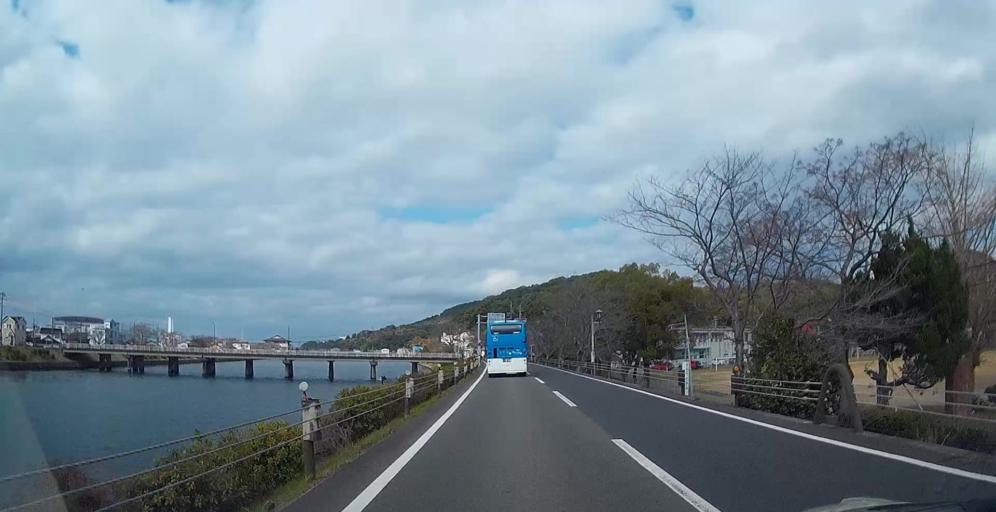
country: JP
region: Kumamoto
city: Minamata
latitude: 32.2132
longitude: 130.4069
